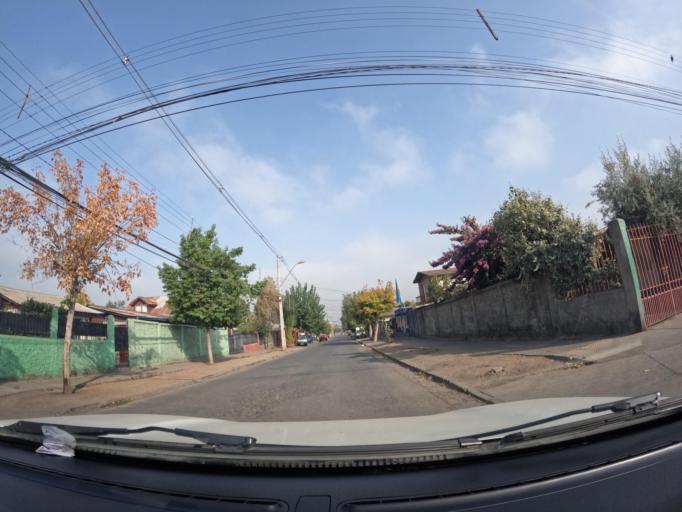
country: CL
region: Santiago Metropolitan
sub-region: Provincia de Santiago
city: Villa Presidente Frei, Nunoa, Santiago, Chile
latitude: -33.4746
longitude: -70.5582
